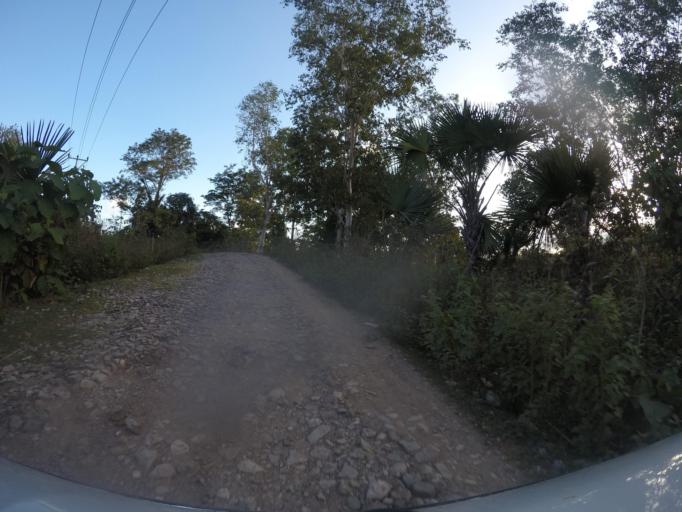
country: TL
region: Baucau
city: Venilale
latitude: -8.7154
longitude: 126.7128
